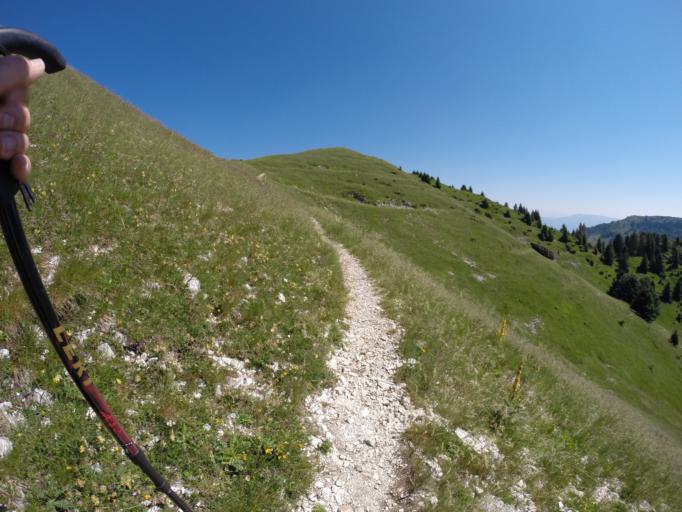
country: IT
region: Veneto
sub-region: Provincia di Treviso
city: Crespano del Grappa
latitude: 45.8856
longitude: 11.8074
